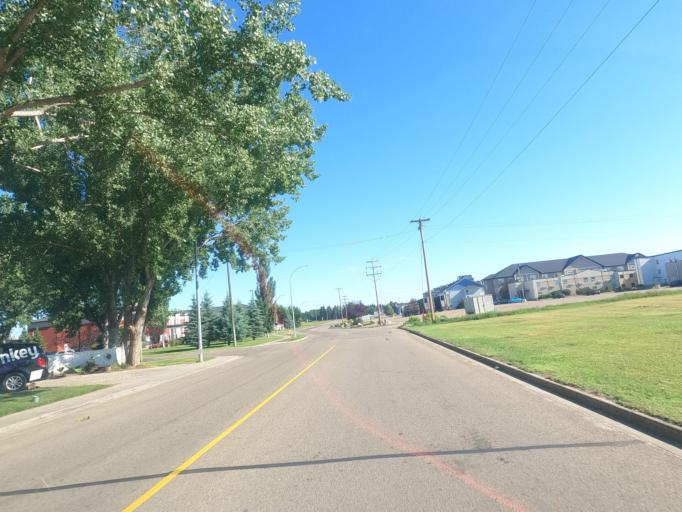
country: CA
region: Alberta
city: Brooks
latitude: 50.5823
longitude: -111.8998
